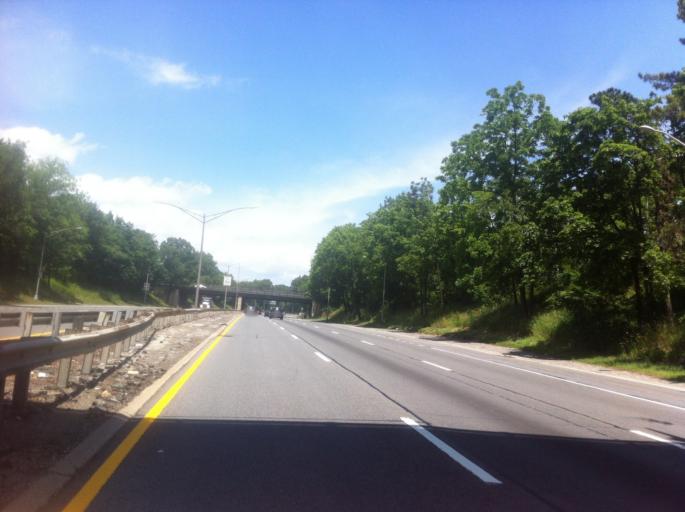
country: US
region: New York
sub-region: Nassau County
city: East Atlantic Beach
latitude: 40.7653
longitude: -73.7804
